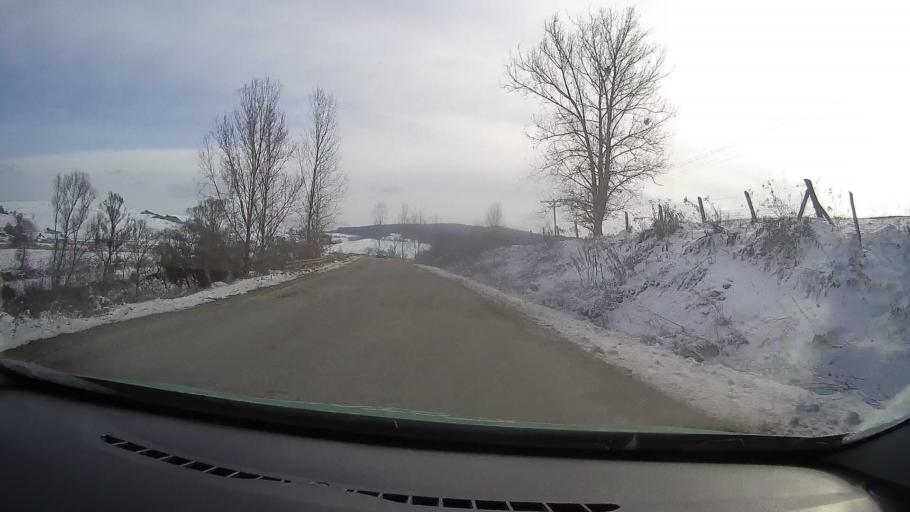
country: RO
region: Sibiu
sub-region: Oras Agnita
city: Ruja
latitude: 46.0009
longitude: 24.6725
